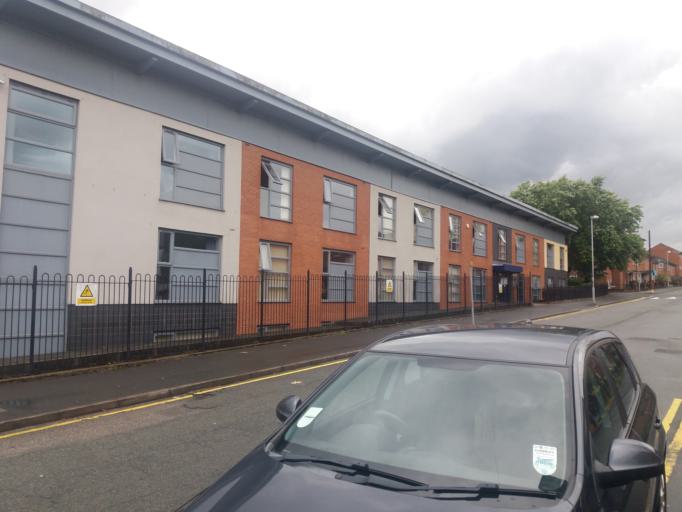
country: GB
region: England
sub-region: Lancashire
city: Preston
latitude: 53.7547
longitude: -2.6934
